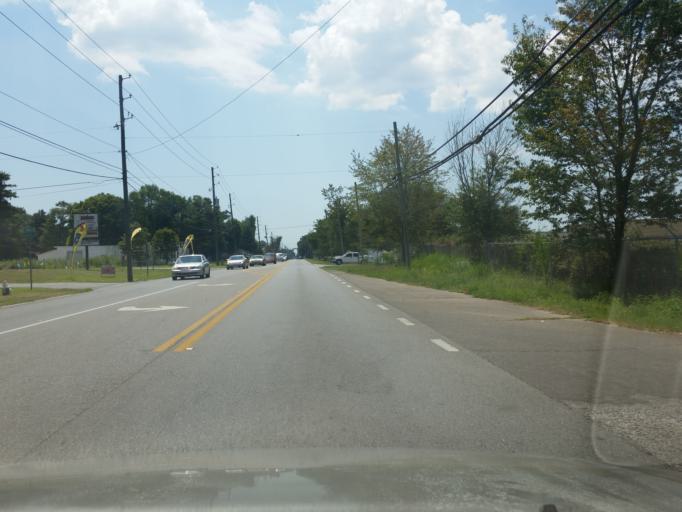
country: US
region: Florida
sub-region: Escambia County
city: Ensley
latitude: 30.5299
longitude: -87.2721
